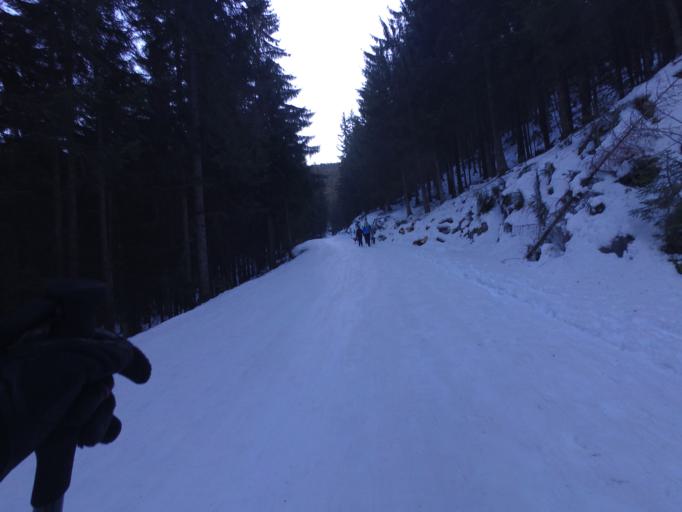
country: AT
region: Salzburg
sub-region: Politischer Bezirk Hallein
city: Scheffau am Tennengebirge
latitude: 47.6387
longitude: 13.2485
